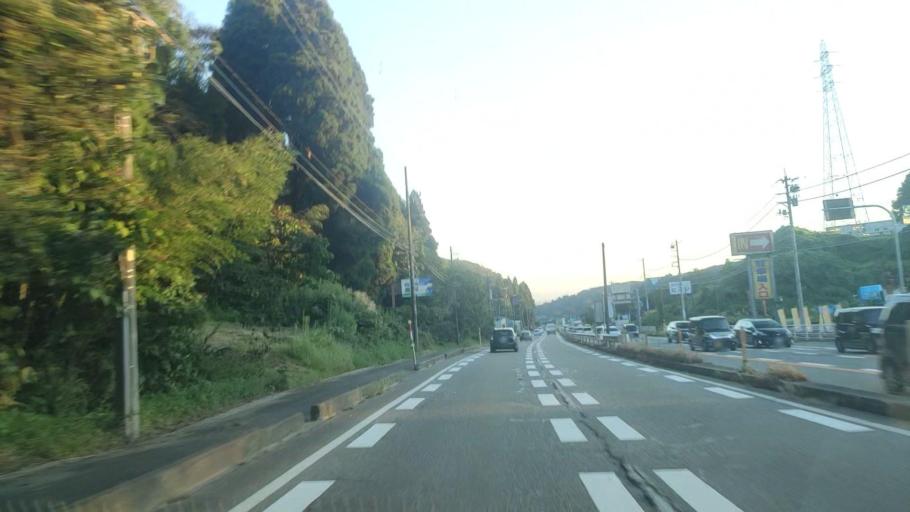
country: JP
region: Toyama
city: Takaoka
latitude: 36.7933
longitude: 137.0020
